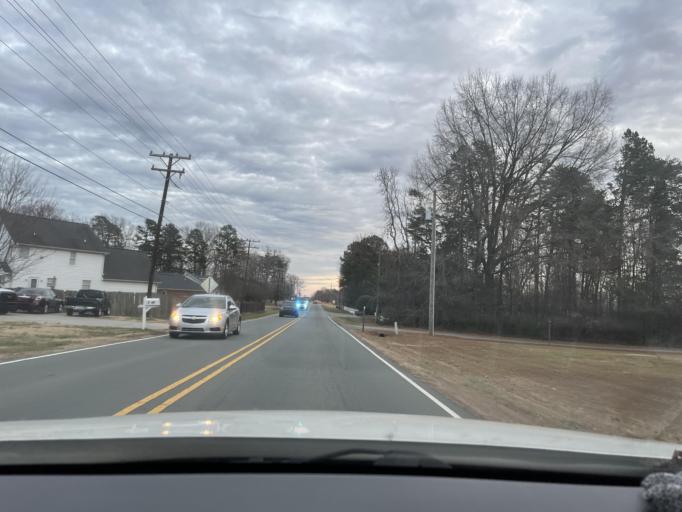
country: US
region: North Carolina
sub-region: Alamance County
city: Elon
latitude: 36.0751
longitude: -79.5112
